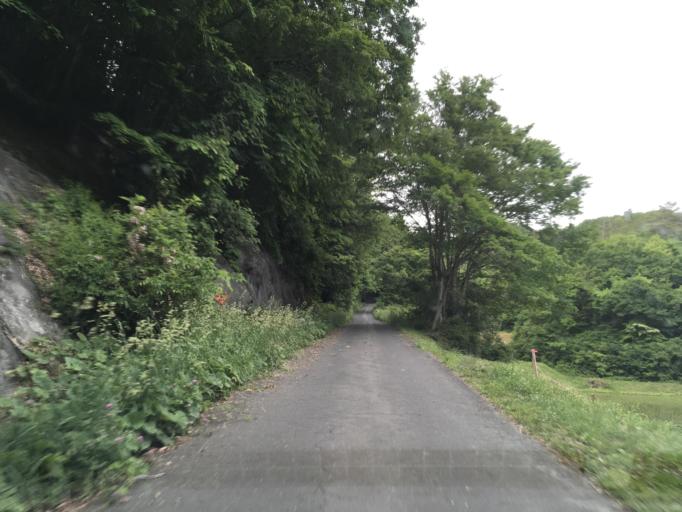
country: JP
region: Iwate
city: Mizusawa
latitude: 39.1222
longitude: 141.2614
